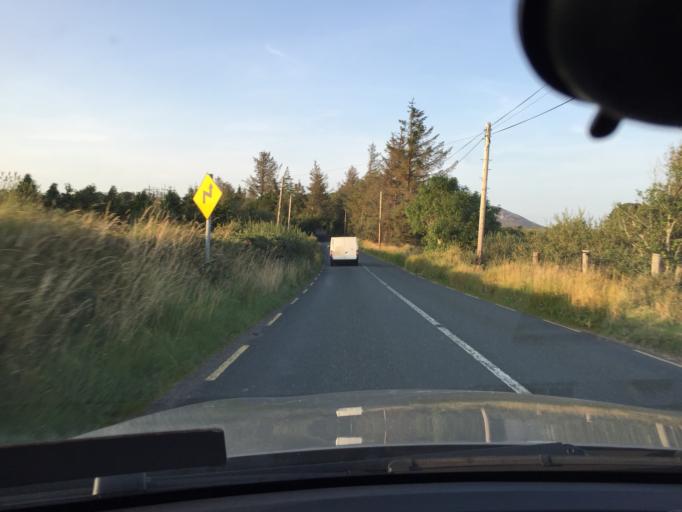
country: IE
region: Leinster
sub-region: Wicklow
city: Kilmacanoge
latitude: 53.1264
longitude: -6.1814
